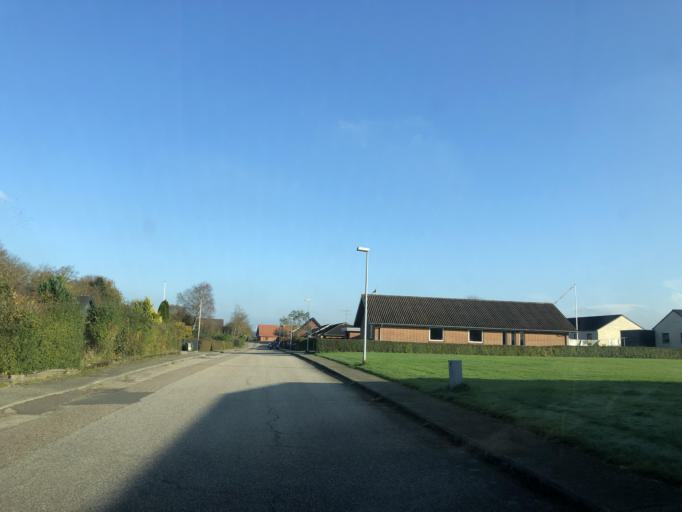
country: DK
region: Central Jutland
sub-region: Holstebro Kommune
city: Vinderup
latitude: 56.4024
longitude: 8.7538
